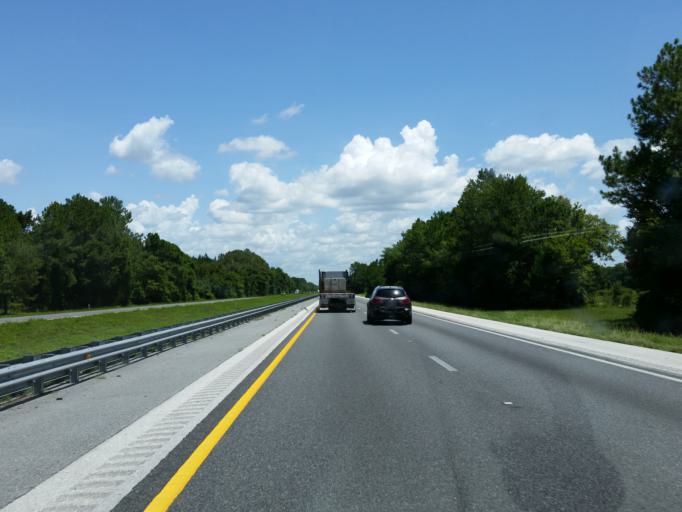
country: US
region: Florida
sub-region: Sumter County
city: Lake Panasoffkee
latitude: 28.8035
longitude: -82.0882
